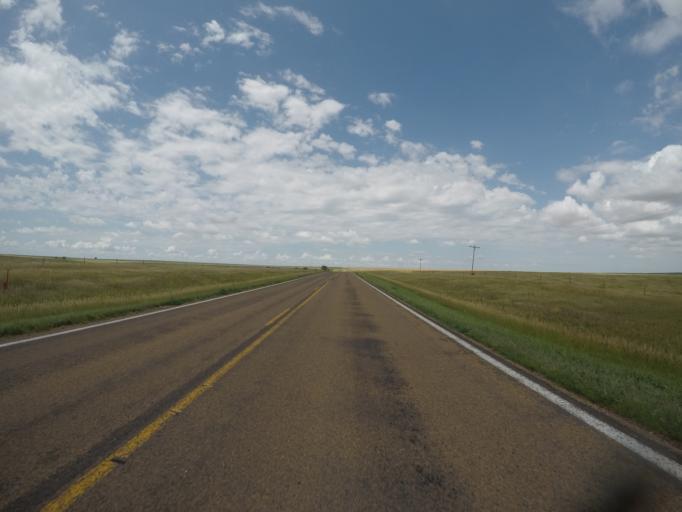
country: US
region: Kansas
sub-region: Rawlins County
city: Atwood
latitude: 39.9487
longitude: -101.0561
